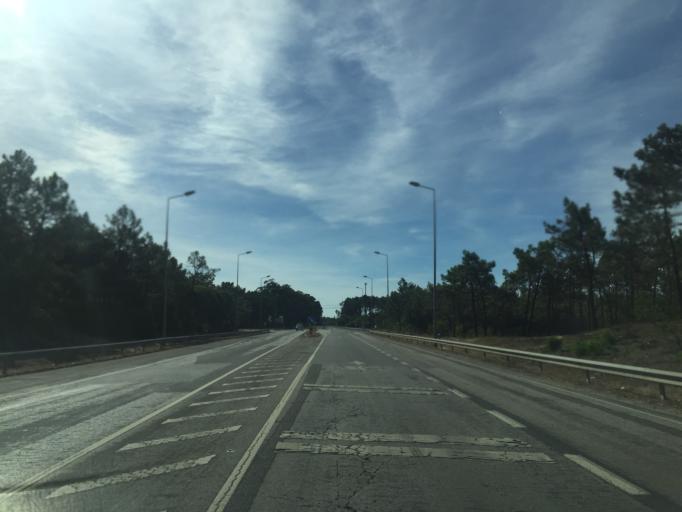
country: PT
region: Coimbra
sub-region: Figueira da Foz
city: Lavos
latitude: 40.0921
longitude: -8.8543
